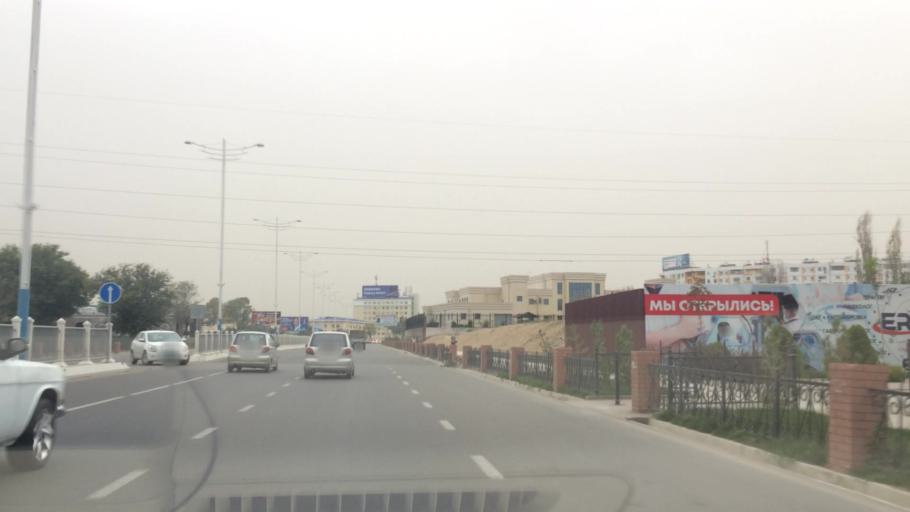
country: UZ
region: Toshkent Shahri
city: Bektemir
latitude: 41.3045
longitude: 69.3110
